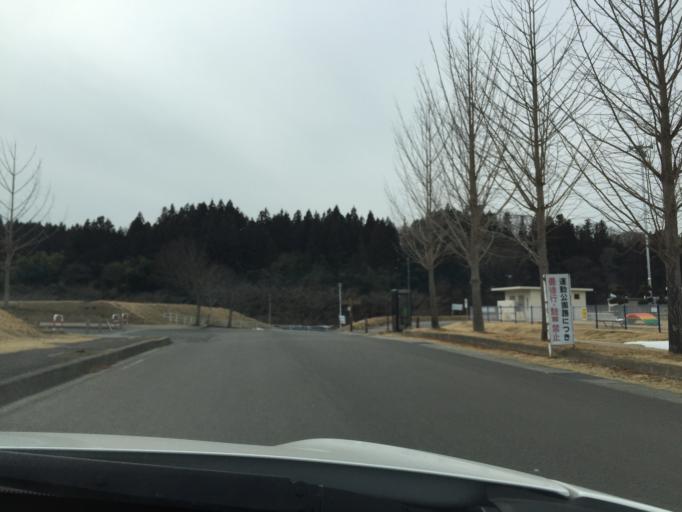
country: JP
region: Fukushima
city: Funehikimachi-funehiki
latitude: 37.2898
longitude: 140.6208
